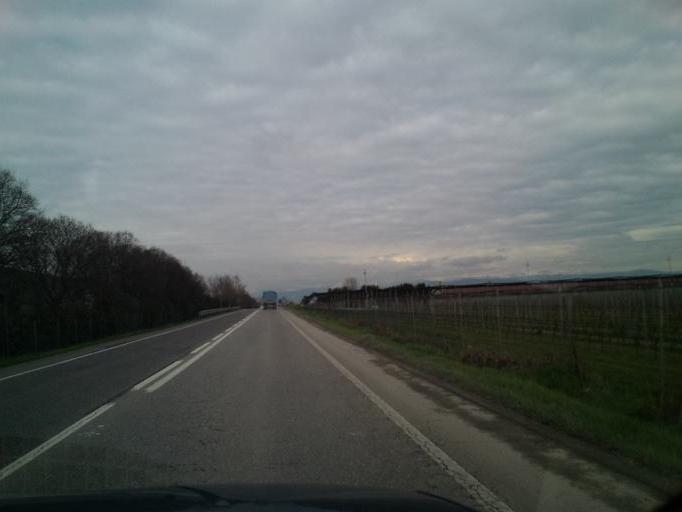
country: IT
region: Veneto
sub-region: Provincia di Verona
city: Sommacampagna
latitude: 45.4036
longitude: 10.8516
